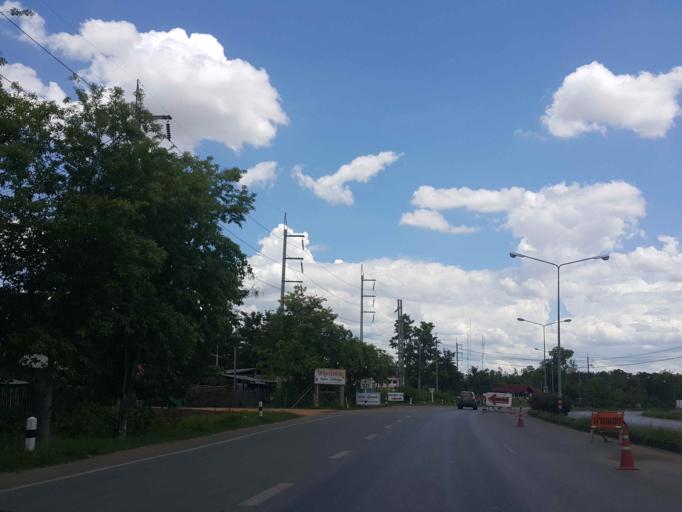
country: TH
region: Phrae
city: Nong Muang Khai
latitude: 18.2104
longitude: 100.1993
